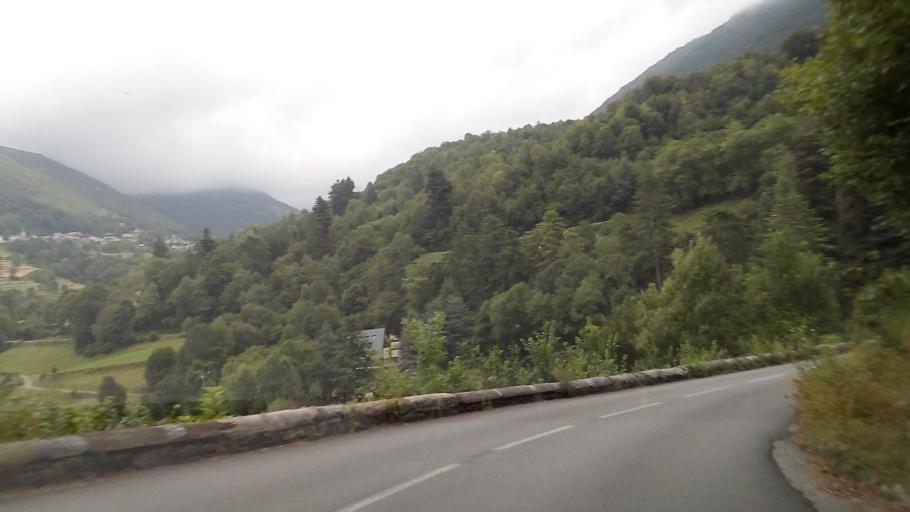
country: FR
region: Aquitaine
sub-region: Departement des Pyrenees-Atlantiques
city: Laruns
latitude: 42.9792
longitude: -0.4220
